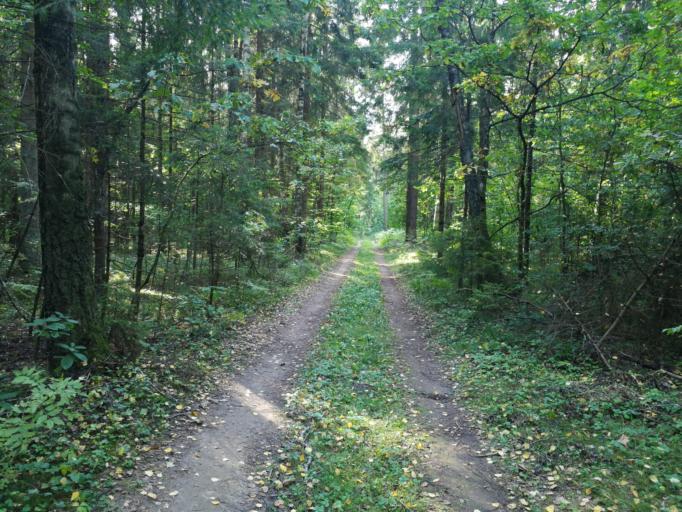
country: BY
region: Mogilev
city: Myazhysyatki
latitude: 53.8287
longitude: 30.1359
